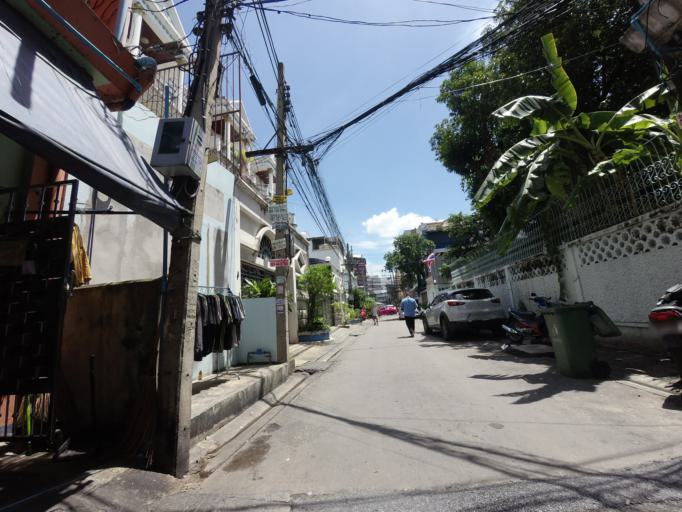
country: TH
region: Bangkok
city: Phaya Thai
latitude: 13.7888
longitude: 100.5598
